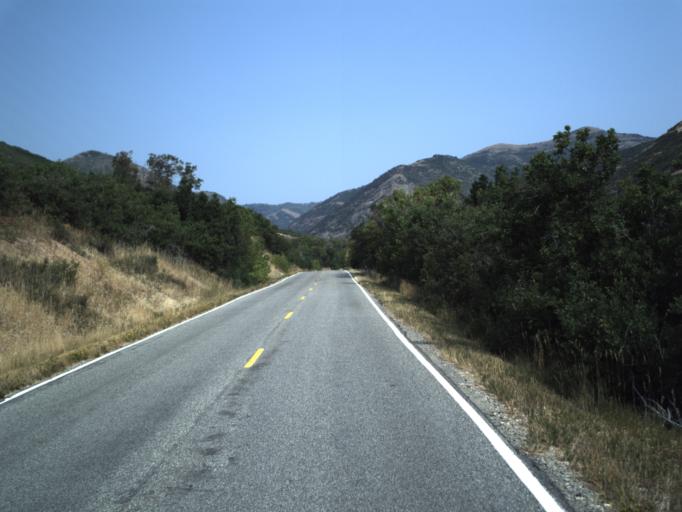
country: US
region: Utah
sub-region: Summit County
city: Summit Park
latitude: 40.7934
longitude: -111.6806
